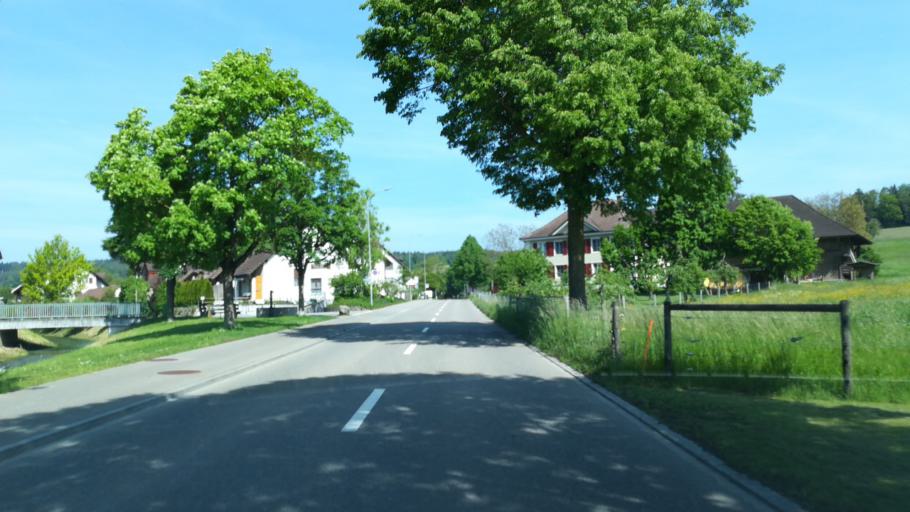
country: CH
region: Thurgau
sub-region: Frauenfeld District
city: Pfyn
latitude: 47.5990
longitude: 8.9529
